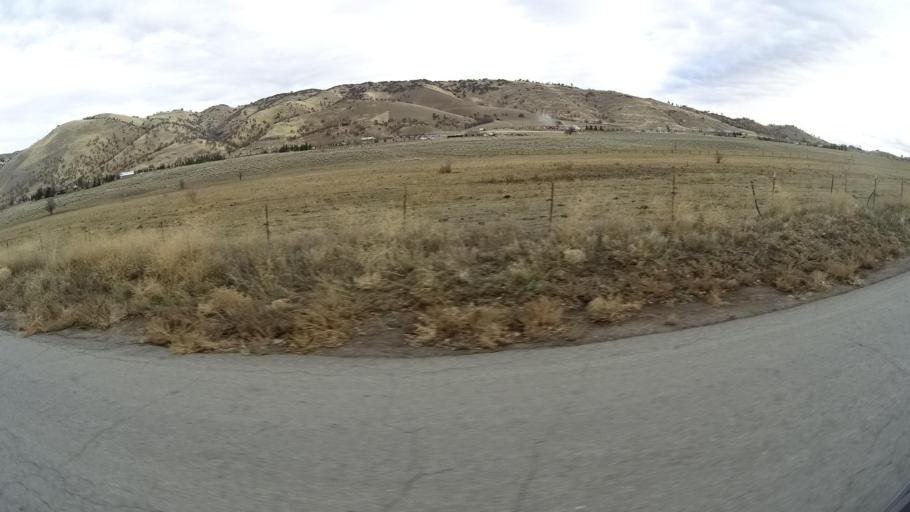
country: US
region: California
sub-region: Kern County
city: Golden Hills
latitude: 35.1219
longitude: -118.5520
